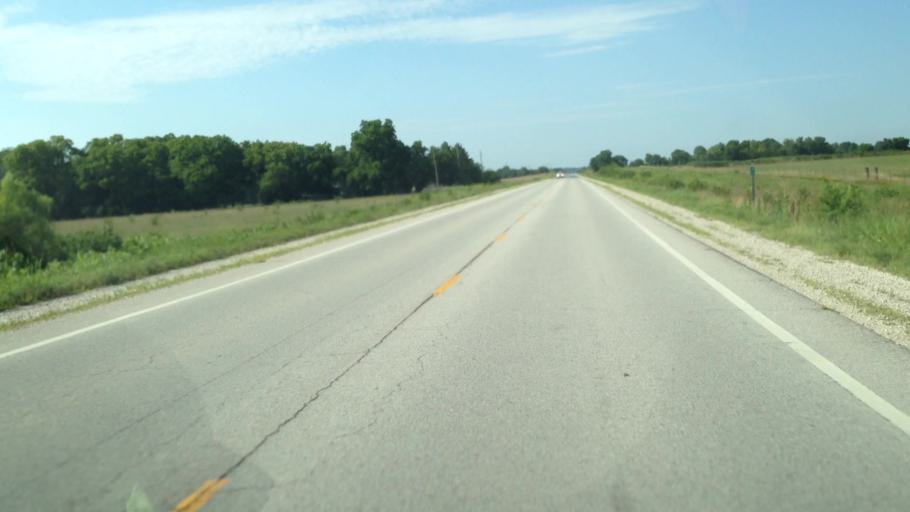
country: US
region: Kansas
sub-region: Neosho County
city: Erie
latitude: 37.4910
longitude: -95.2693
